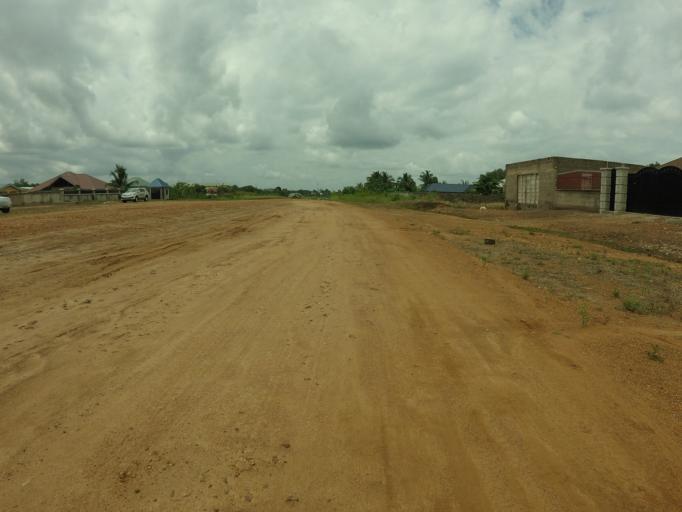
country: GH
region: Volta
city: Ho
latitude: 6.5837
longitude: 0.4598
